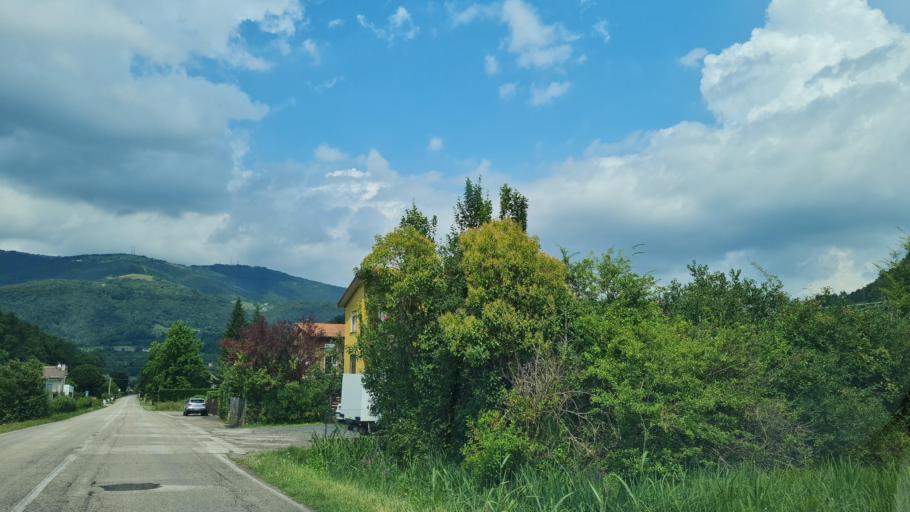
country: IT
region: Veneto
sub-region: Provincia di Vicenza
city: Marostica
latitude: 45.7571
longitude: 11.6605
